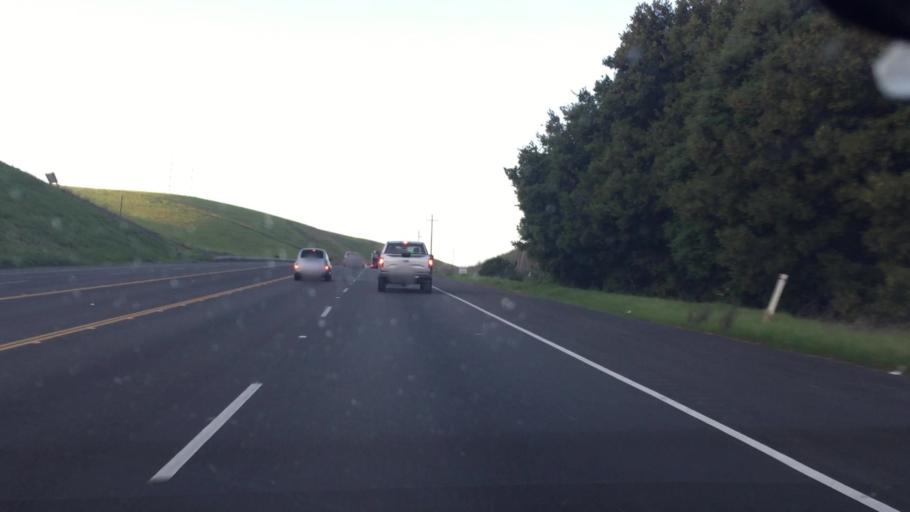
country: US
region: California
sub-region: Alameda County
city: Livermore
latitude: 37.6226
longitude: -121.8090
